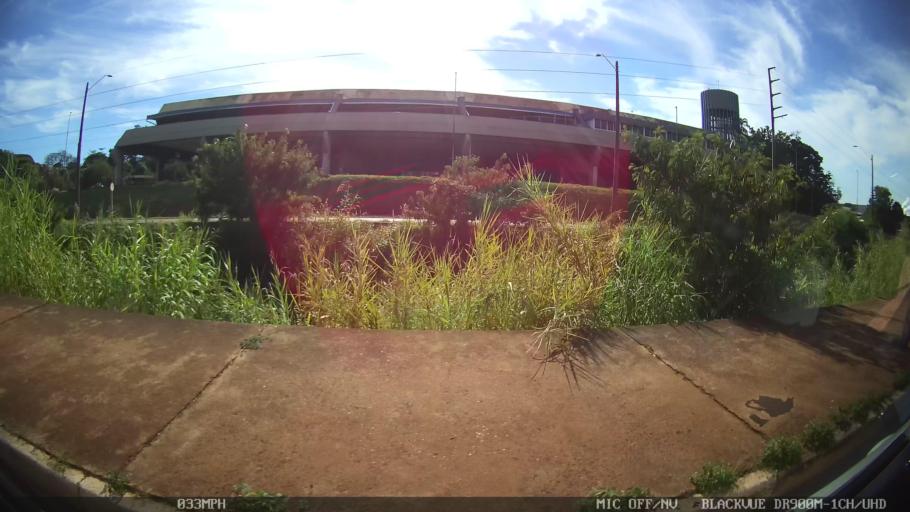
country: BR
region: Sao Paulo
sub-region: Araraquara
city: Araraquara
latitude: -21.8077
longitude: -48.1737
